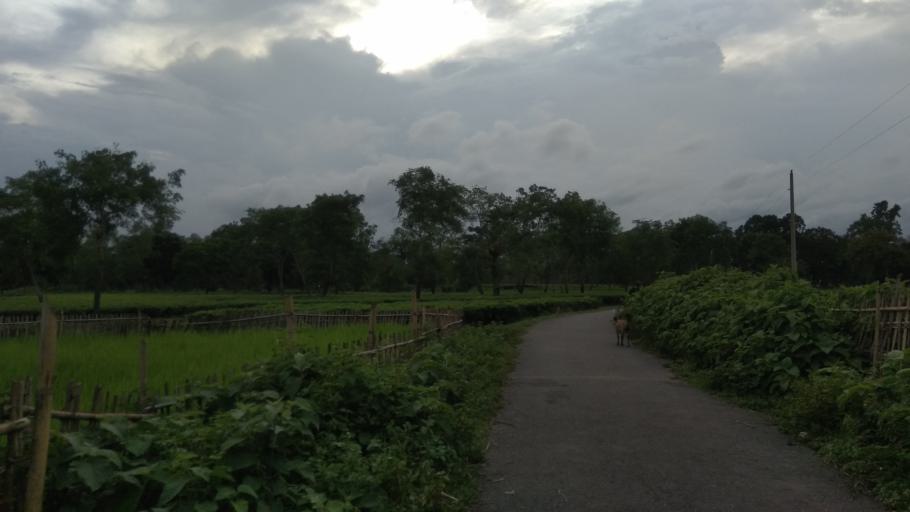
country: IN
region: Tripura
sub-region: Dhalai
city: Kamalpur
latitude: 24.1760
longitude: 91.8798
